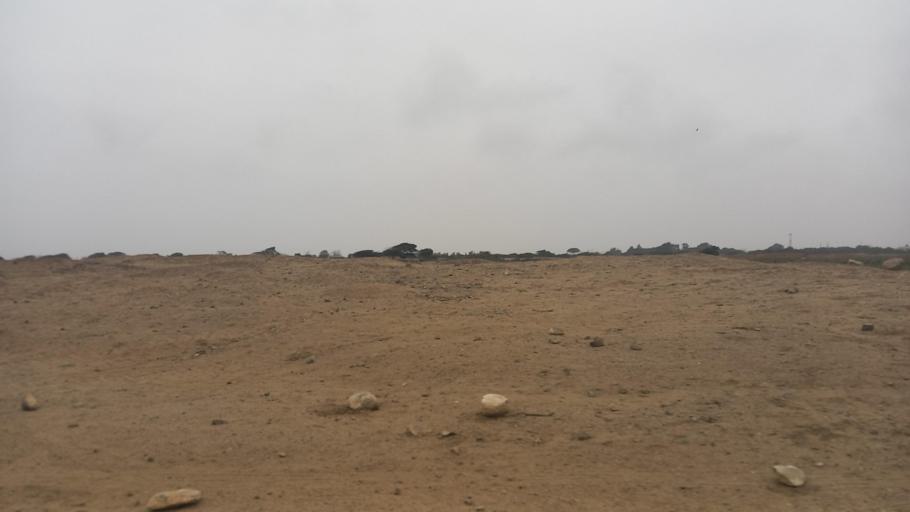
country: PE
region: La Libertad
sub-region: Provincia de Trujillo
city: La Esperanza
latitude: -8.0987
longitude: -79.0778
